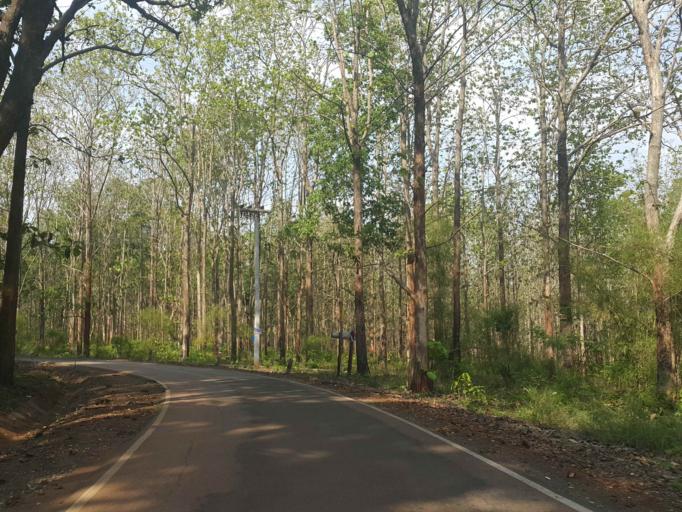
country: TH
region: Chiang Mai
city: Mae Taeng
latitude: 19.0752
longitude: 99.0863
